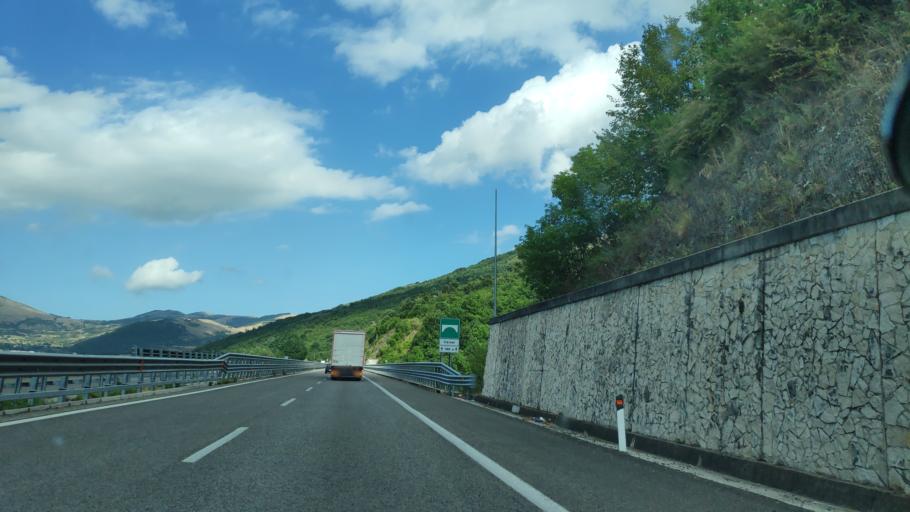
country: IT
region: Campania
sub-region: Provincia di Salerno
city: Pertosa
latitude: 40.5314
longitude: 15.4443
